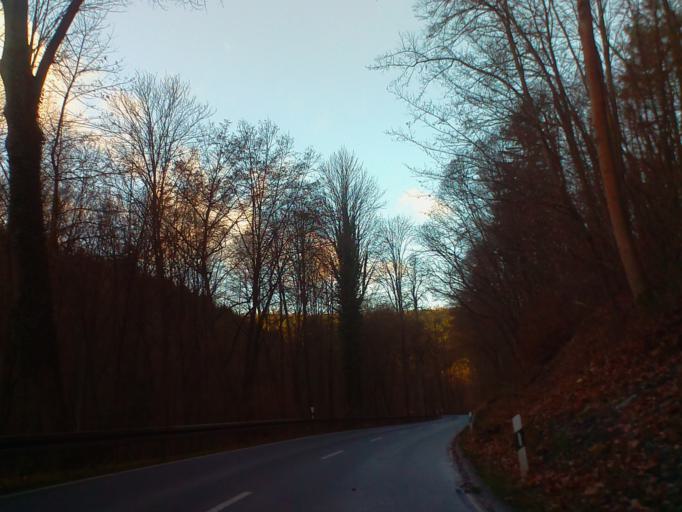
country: DE
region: Thuringia
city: Schwarzburg
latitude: 50.6634
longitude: 11.2261
